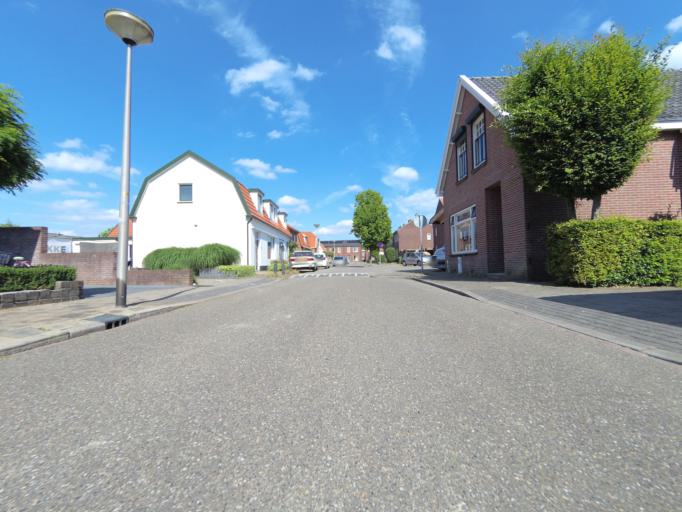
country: NL
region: Overijssel
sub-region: Gemeente Oldenzaal
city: Oldenzaal
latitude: 52.3158
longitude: 6.9227
